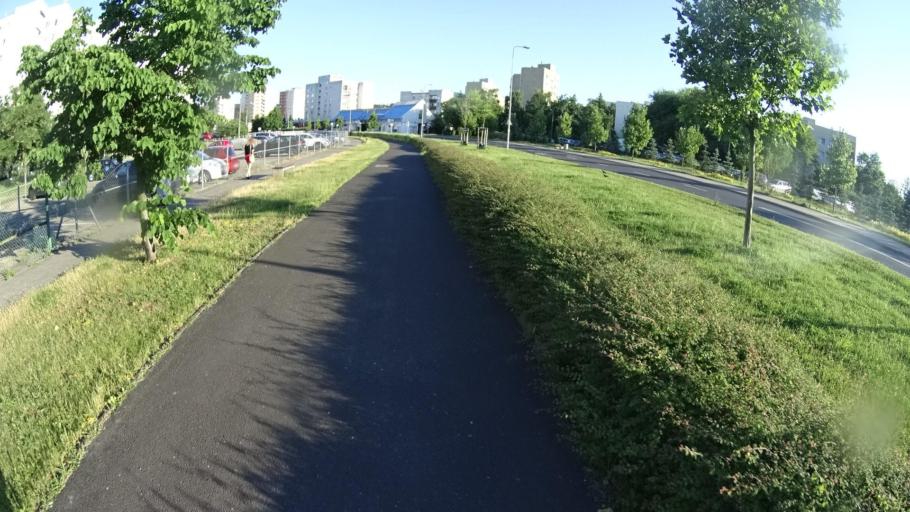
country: PL
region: Masovian Voivodeship
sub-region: Warszawa
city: Bemowo
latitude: 52.2593
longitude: 20.9177
